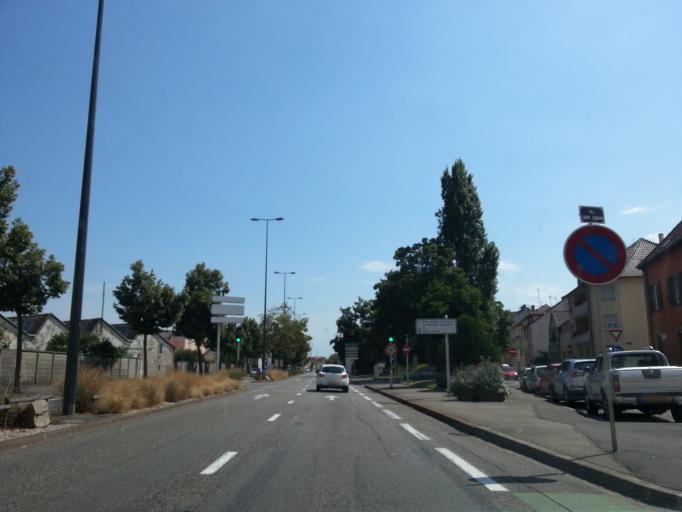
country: FR
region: Alsace
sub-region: Departement du Haut-Rhin
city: Colmar
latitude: 48.0785
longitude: 7.3652
